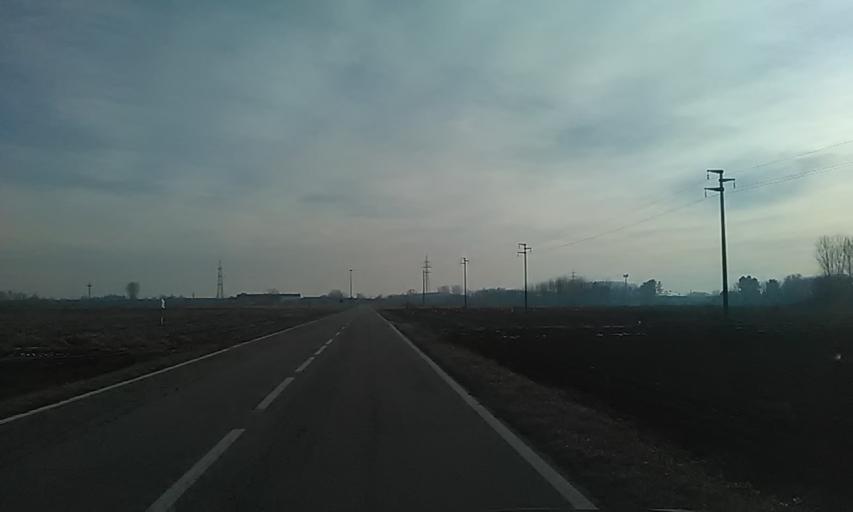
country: IT
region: Piedmont
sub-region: Provincia di Novara
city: Recetto
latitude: 45.4716
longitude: 8.4301
